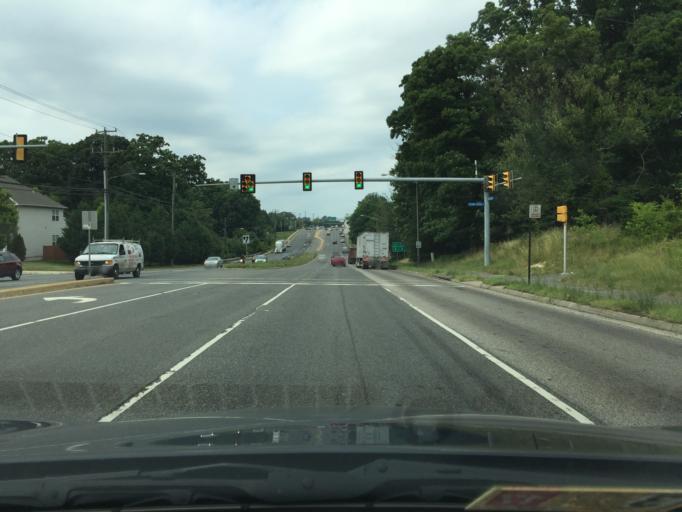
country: US
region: Virginia
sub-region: Fairfax County
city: Franconia
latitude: 38.7877
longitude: -77.1365
